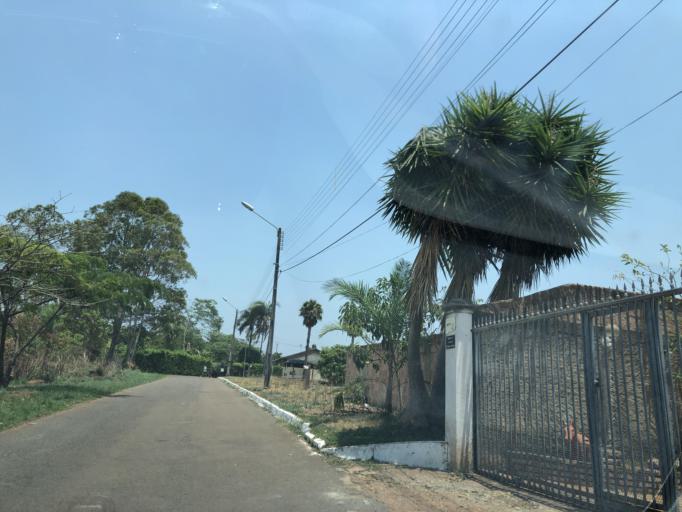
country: BR
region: Federal District
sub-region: Brasilia
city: Brasilia
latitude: -15.9360
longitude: -47.9407
